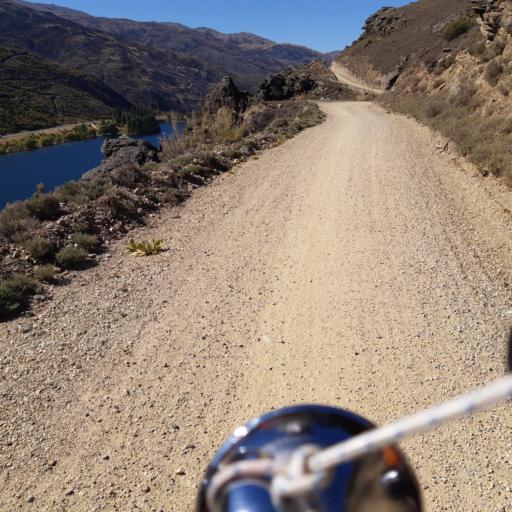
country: NZ
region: Otago
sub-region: Queenstown-Lakes District
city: Wanaka
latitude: -45.0846
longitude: 169.2505
